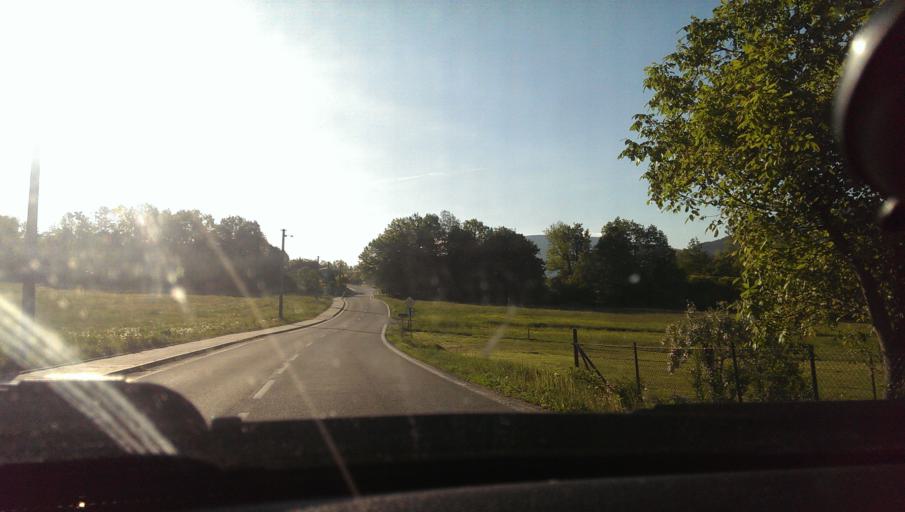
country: CZ
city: Kuncice pod Ondrejnikem
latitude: 49.5408
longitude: 18.2831
